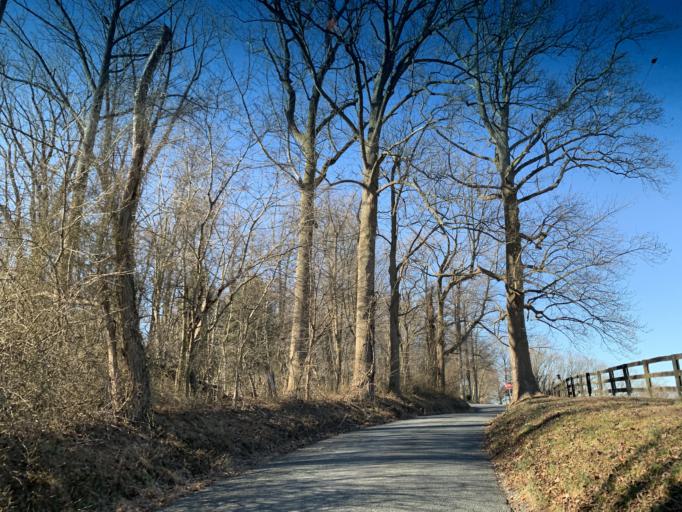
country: US
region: Maryland
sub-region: Harford County
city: Aberdeen
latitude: 39.6099
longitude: -76.2215
